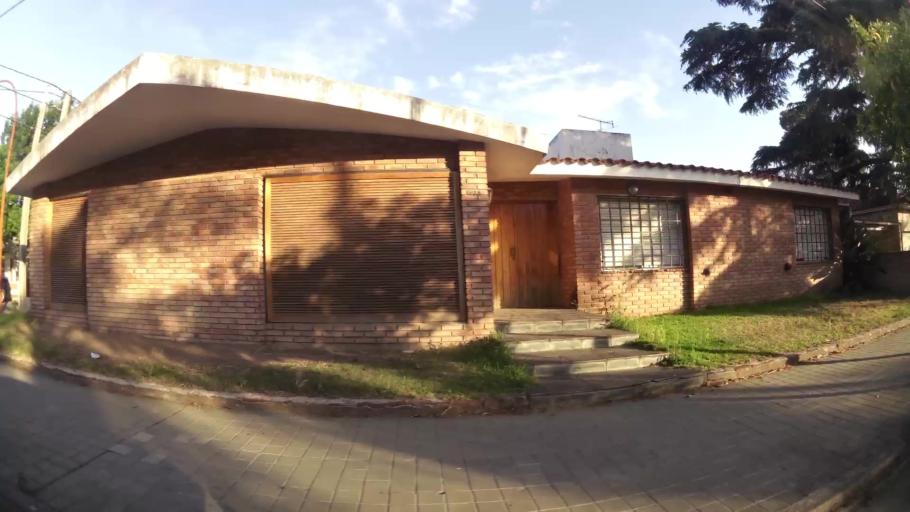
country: AR
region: Cordoba
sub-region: Departamento de Capital
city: Cordoba
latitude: -31.3776
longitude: -64.2330
